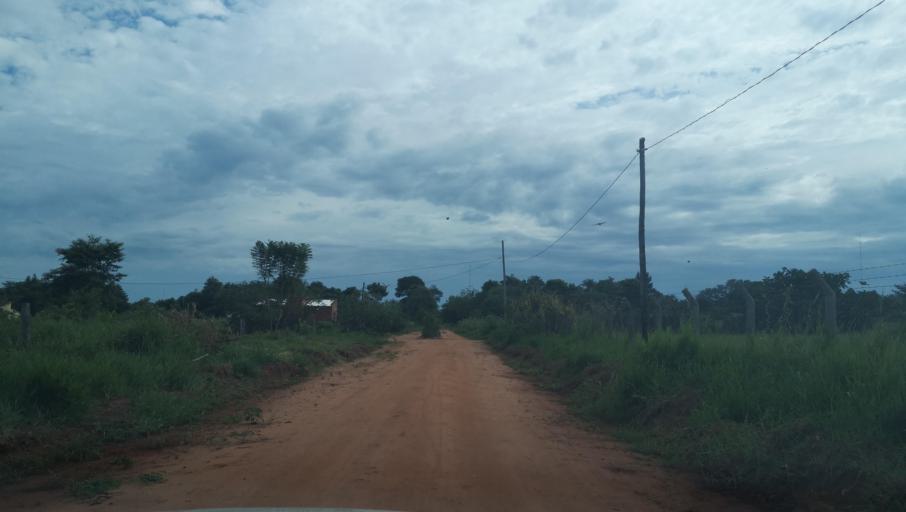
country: PY
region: San Pedro
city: Capiibary
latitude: -24.7245
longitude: -56.0210
